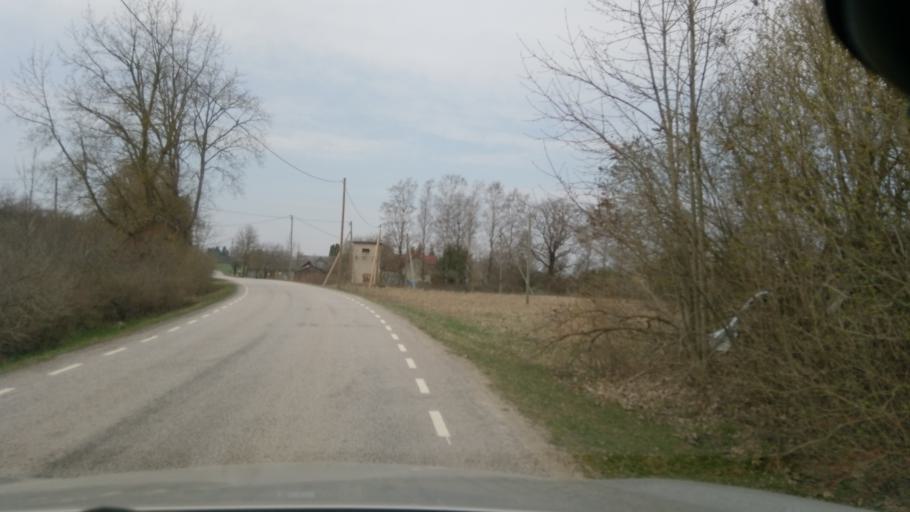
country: EE
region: Jaervamaa
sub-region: Tueri vald
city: Sarevere
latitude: 58.7810
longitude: 25.4809
